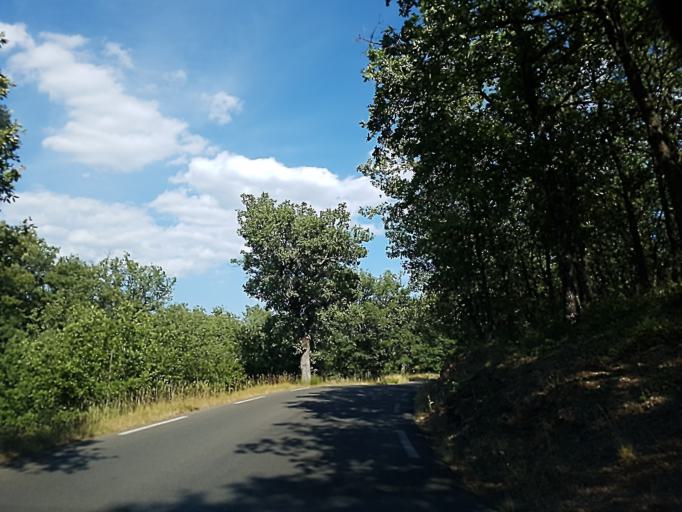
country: FR
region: Provence-Alpes-Cote d'Azur
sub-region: Departement du Var
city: Bras
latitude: 43.4597
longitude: 5.9156
